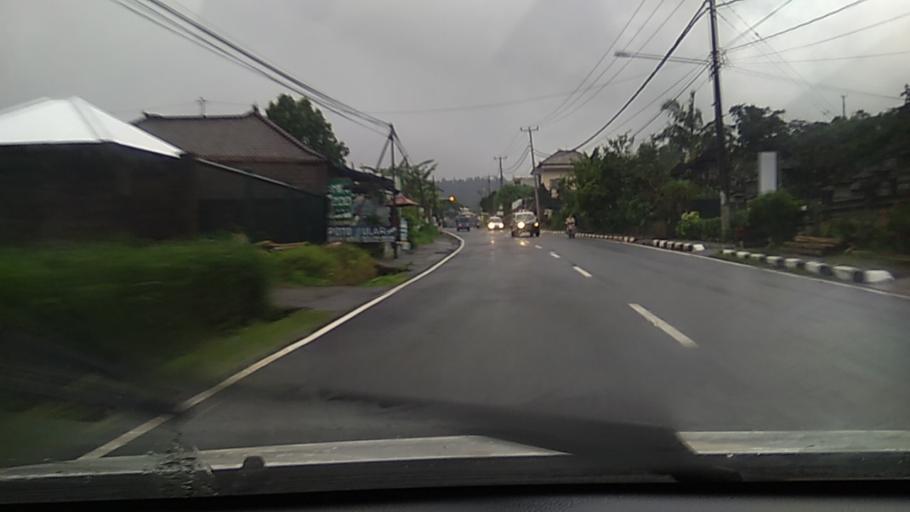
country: ID
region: Bali
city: Munduk
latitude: -8.2734
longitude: 115.1637
